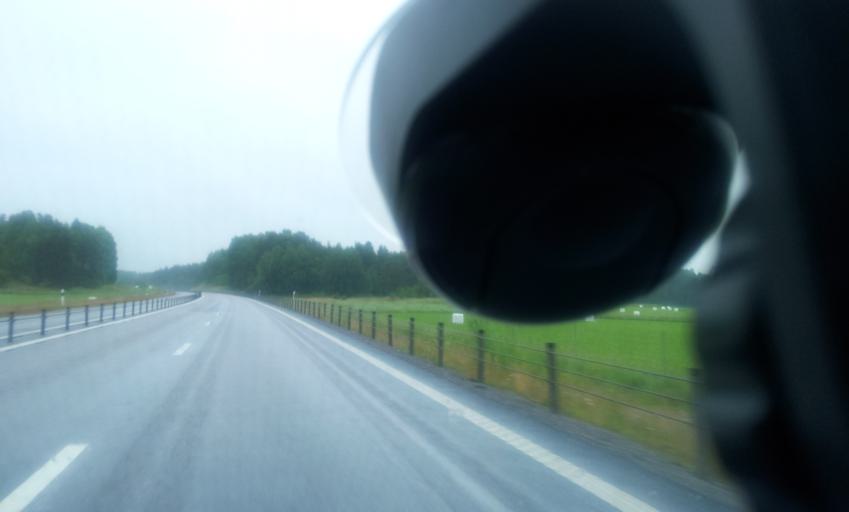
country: SE
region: OEstergoetland
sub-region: Soderkopings Kommun
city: Soederkoeping
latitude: 58.4118
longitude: 16.4012
